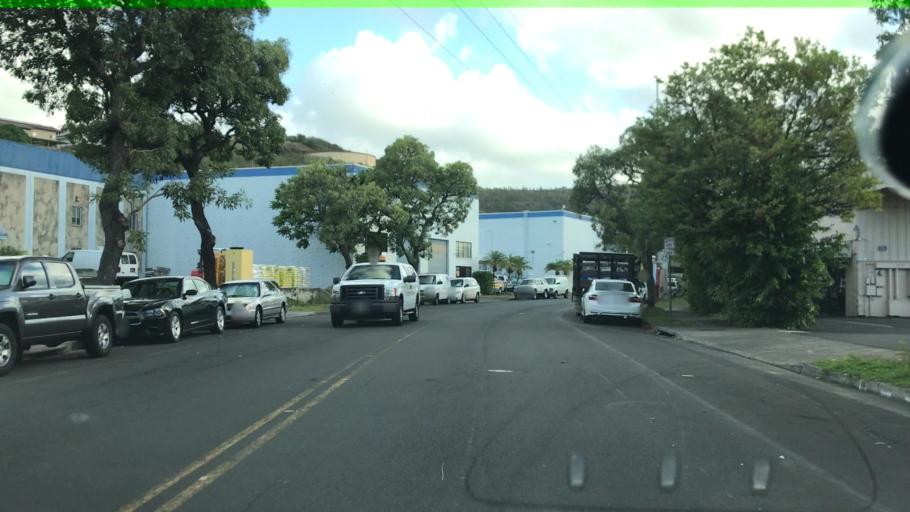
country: US
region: Hawaii
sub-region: Honolulu County
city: Halawa Heights
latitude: 21.3738
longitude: -157.9131
